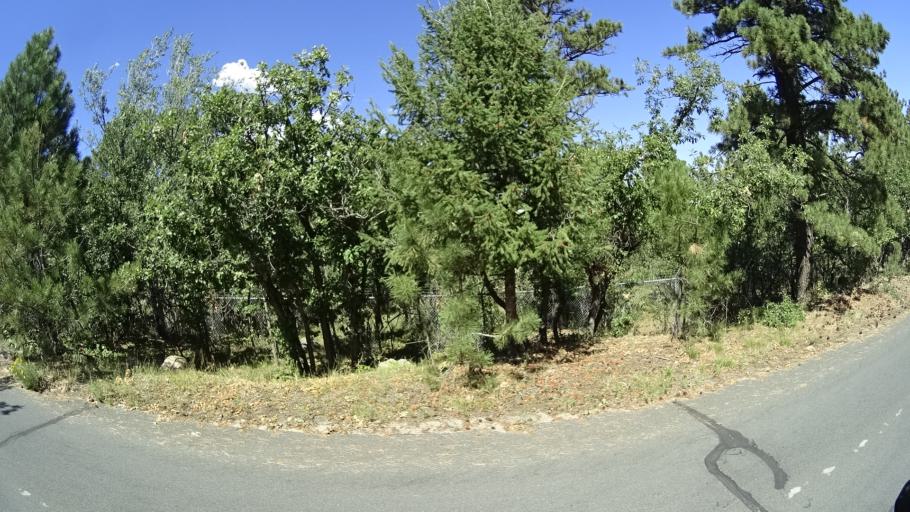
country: US
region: Colorado
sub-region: El Paso County
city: Colorado Springs
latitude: 38.7750
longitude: -104.8461
